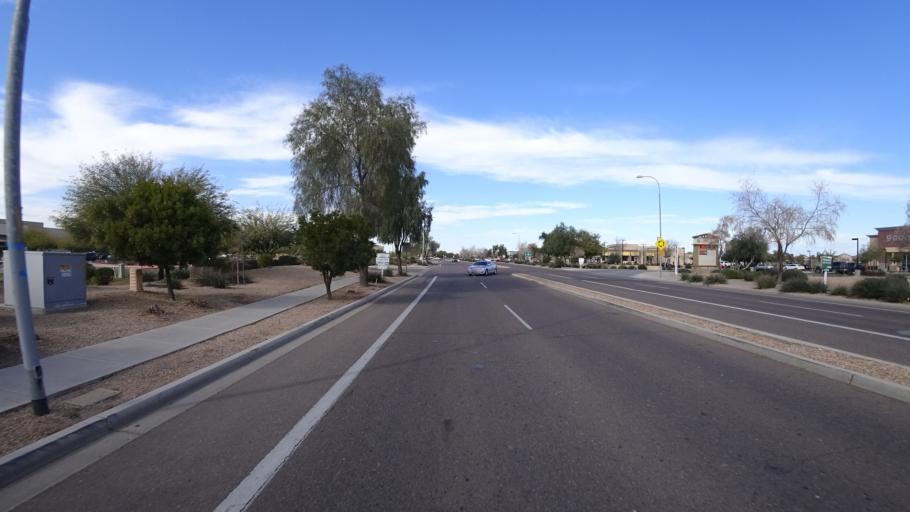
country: US
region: Arizona
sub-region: Maricopa County
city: Tolleson
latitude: 33.4191
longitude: -112.2727
